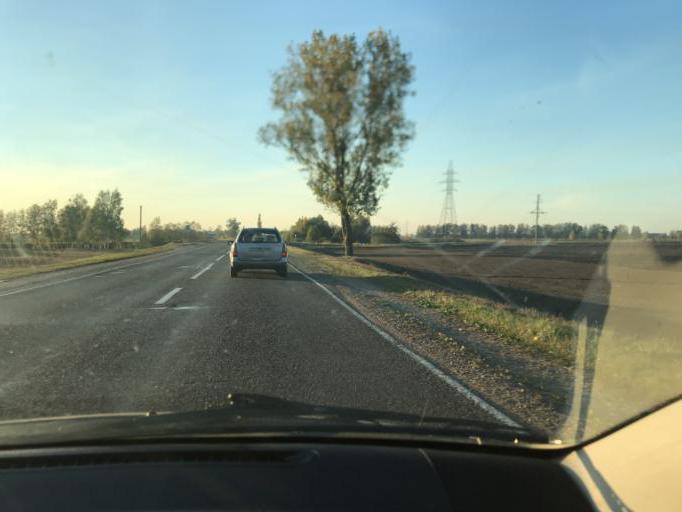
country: BY
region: Brest
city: Pinsk
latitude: 52.0695
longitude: 26.1811
